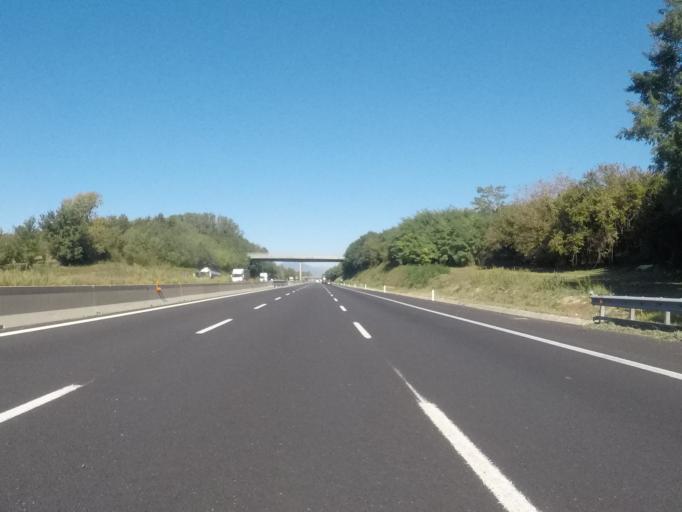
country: IT
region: Campania
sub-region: Provincia di Caserta
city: Santa Lucia
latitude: 41.3254
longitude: 14.0782
